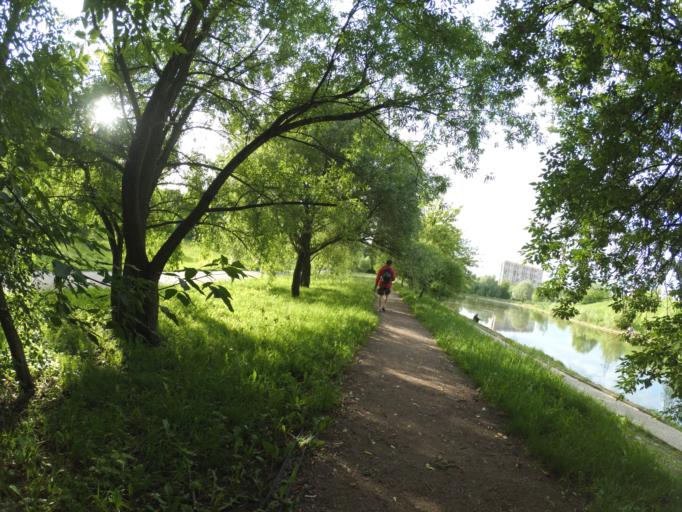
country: RU
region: Moscow
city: Ramenki
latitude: 55.6798
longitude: 37.5084
